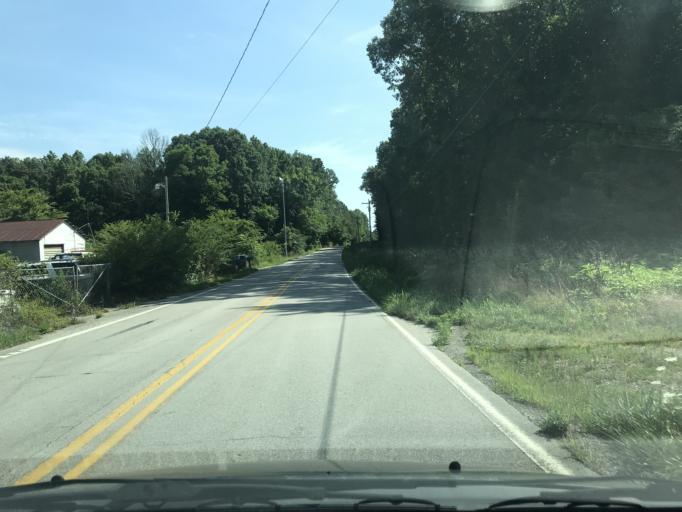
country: US
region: Tennessee
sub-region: Hamilton County
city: Sale Creek
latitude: 35.3103
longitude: -85.0324
